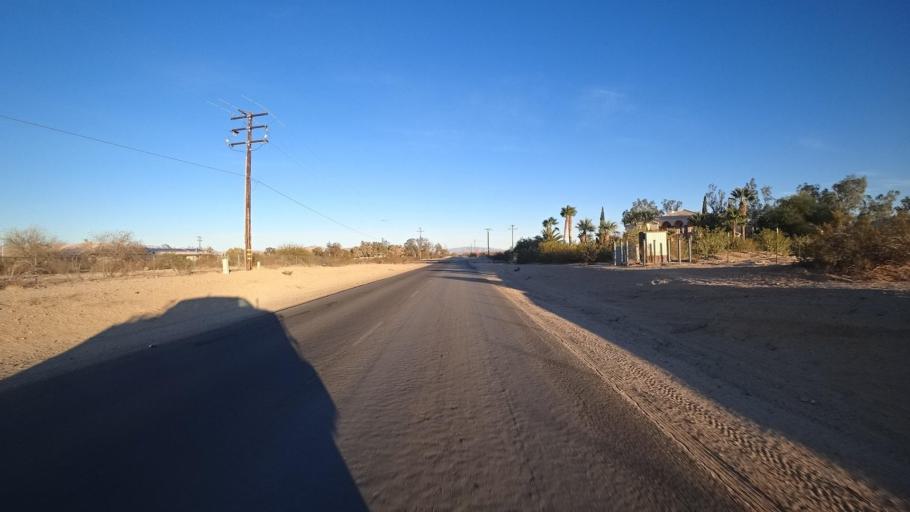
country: US
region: California
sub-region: Kern County
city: Ridgecrest
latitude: 35.6298
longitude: -117.7069
